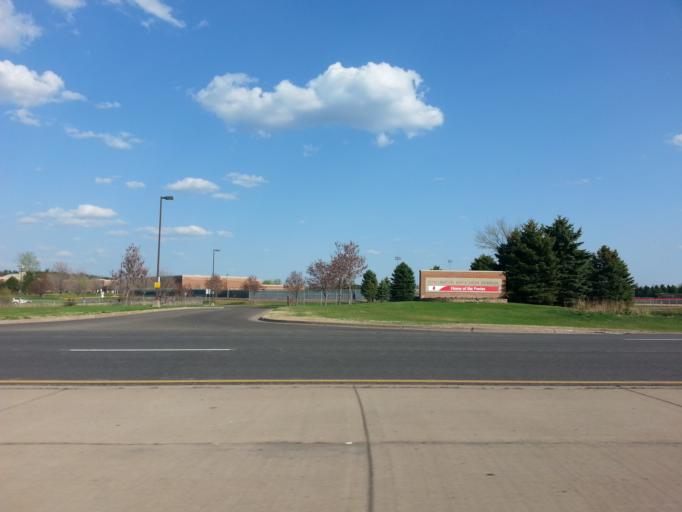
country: US
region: Minnesota
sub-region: Washington County
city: Lake Elmo
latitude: 45.0304
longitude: -92.8524
